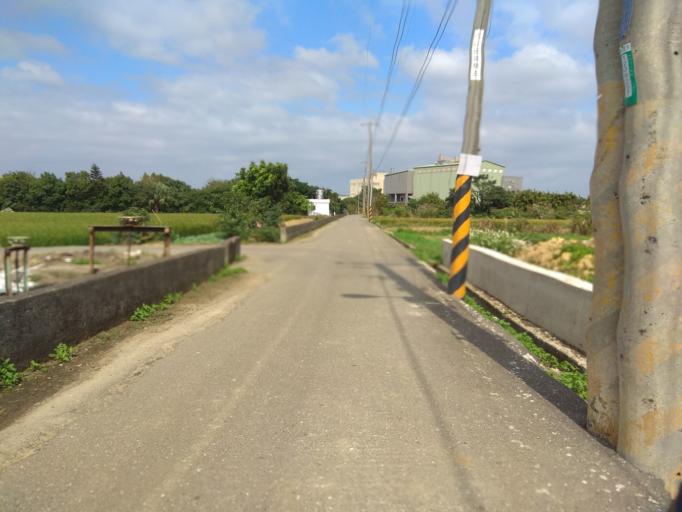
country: TW
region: Taiwan
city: Taoyuan City
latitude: 25.0735
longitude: 121.2489
